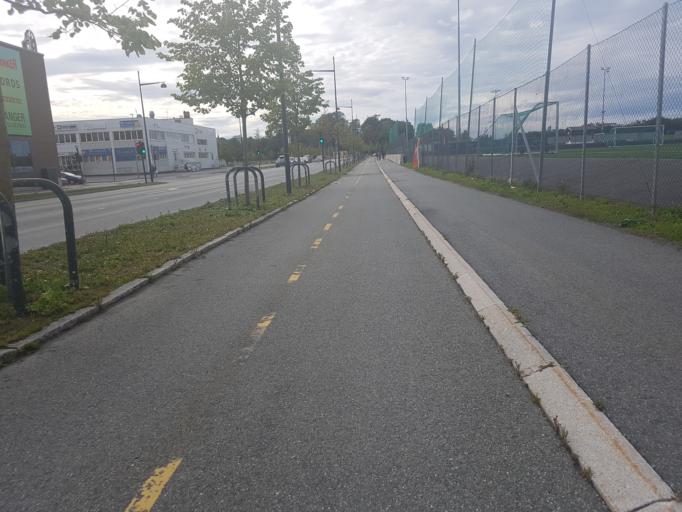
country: NO
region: Sor-Trondelag
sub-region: Trondheim
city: Trondheim
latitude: 63.4446
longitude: 10.4474
